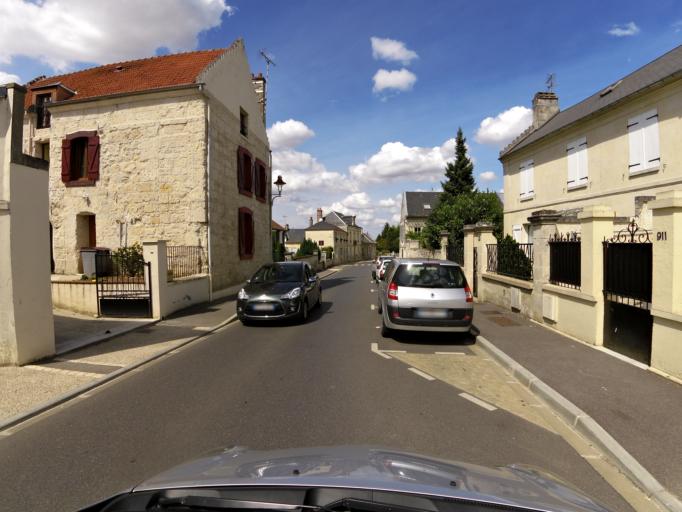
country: FR
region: Picardie
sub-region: Departement de l'Aisne
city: Courmelles
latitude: 49.3453
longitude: 3.3118
